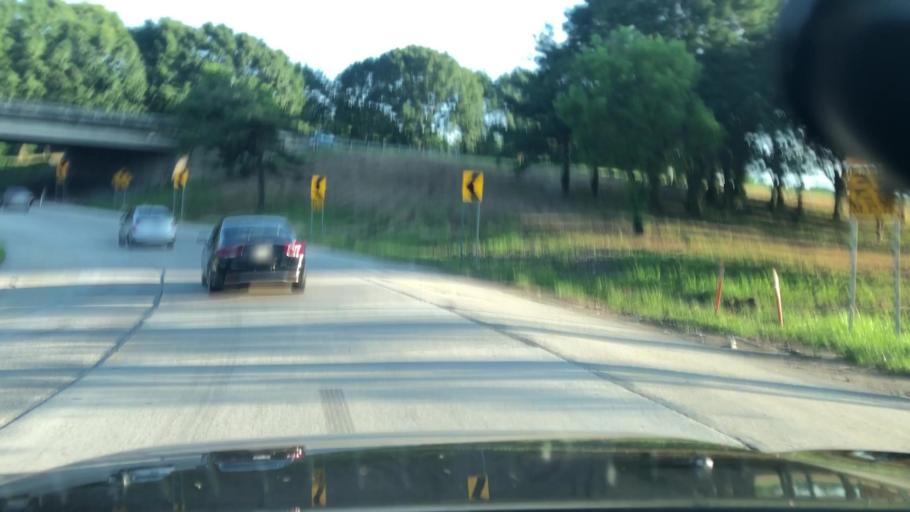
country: US
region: Pennsylvania
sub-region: Montgomery County
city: West Conshohocken
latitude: 40.0653
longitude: -75.3238
